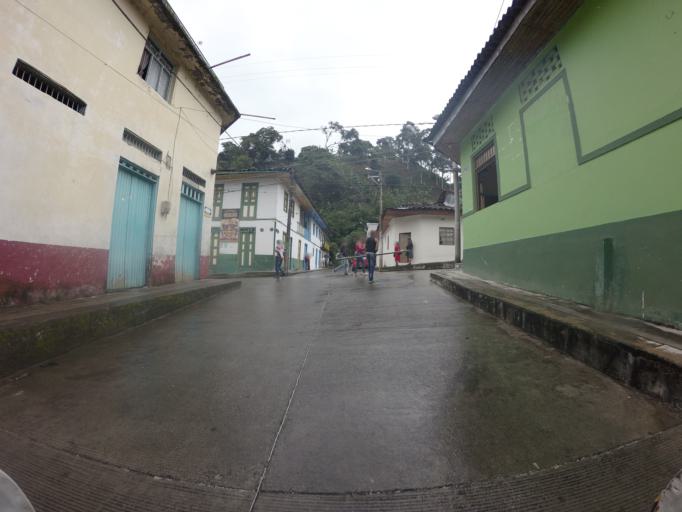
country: CO
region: Quindio
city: Genova
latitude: 4.2051
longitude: -75.7920
